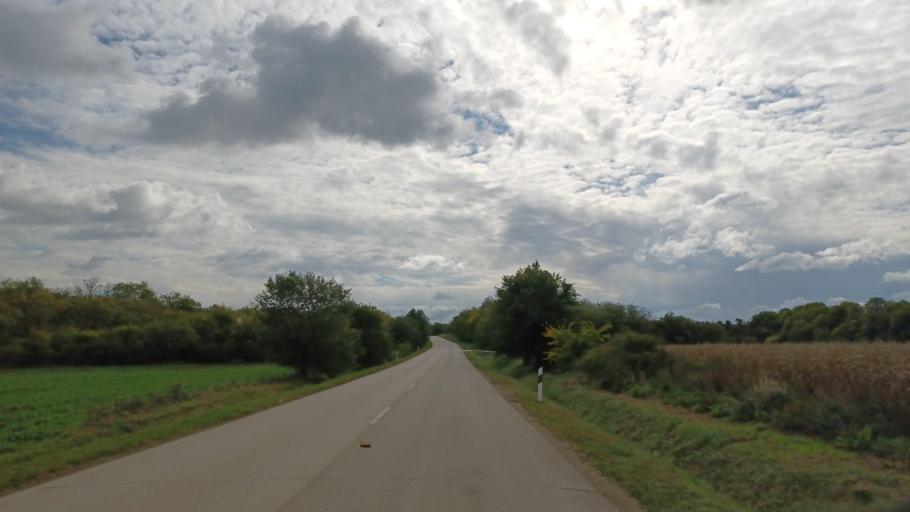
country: HU
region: Tolna
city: Simontornya
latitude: 46.7325
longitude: 18.5677
